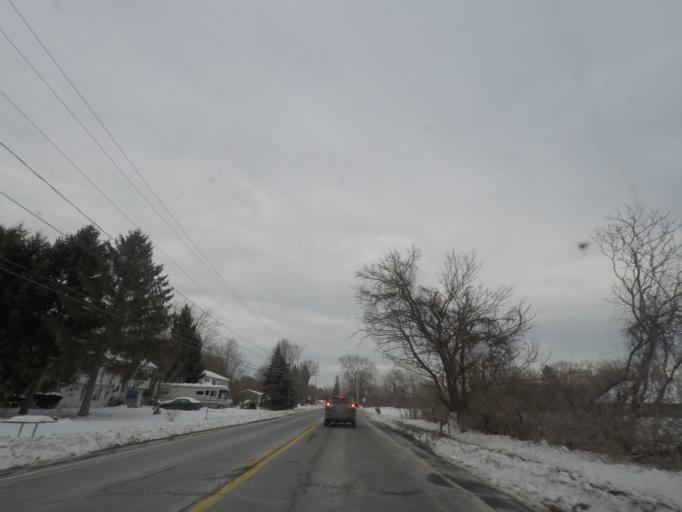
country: US
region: New York
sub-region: Greene County
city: Coxsackie
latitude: 42.3514
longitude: -73.7437
